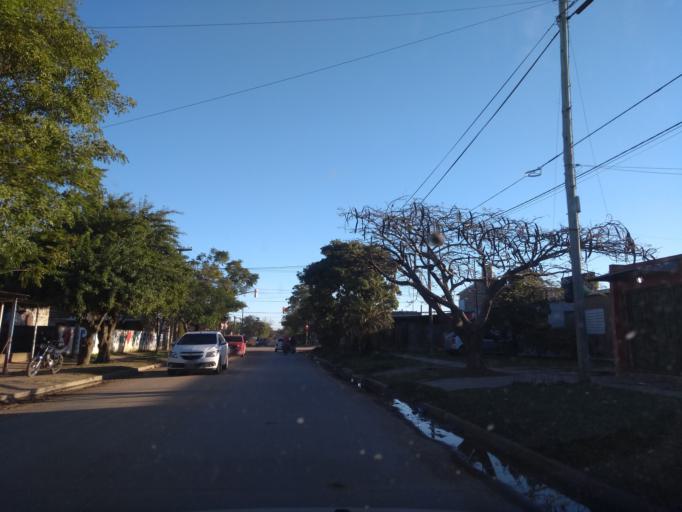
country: AR
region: Chaco
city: Puerto Vilelas
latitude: -27.4969
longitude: -58.9570
